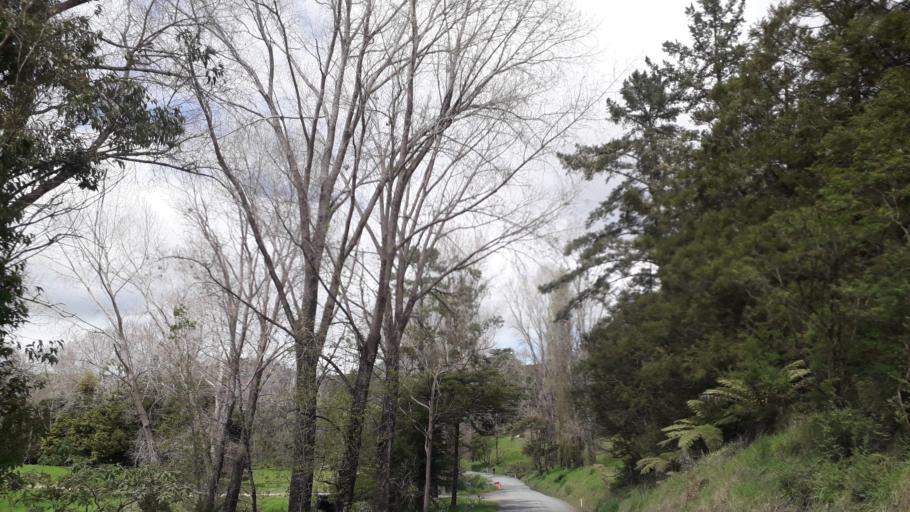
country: NZ
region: Northland
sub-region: Far North District
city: Taipa
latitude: -35.0911
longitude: 173.5149
